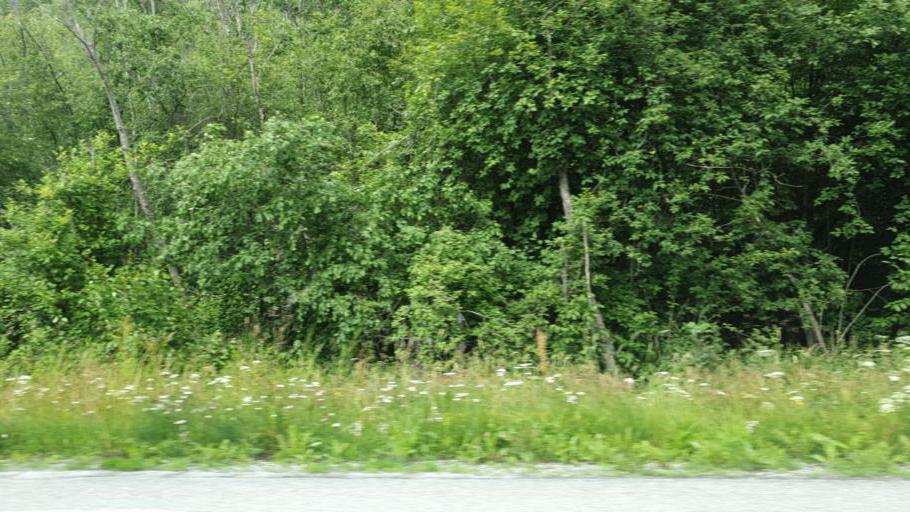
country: NO
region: Oppland
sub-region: Sel
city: Otta
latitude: 61.8425
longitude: 9.3882
